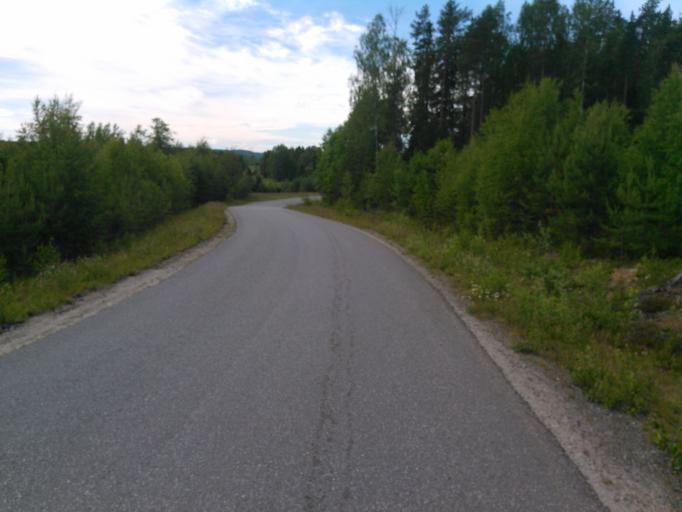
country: SE
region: Vaesterbotten
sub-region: Vannas Kommun
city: Vannasby
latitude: 63.8922
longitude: 19.9854
